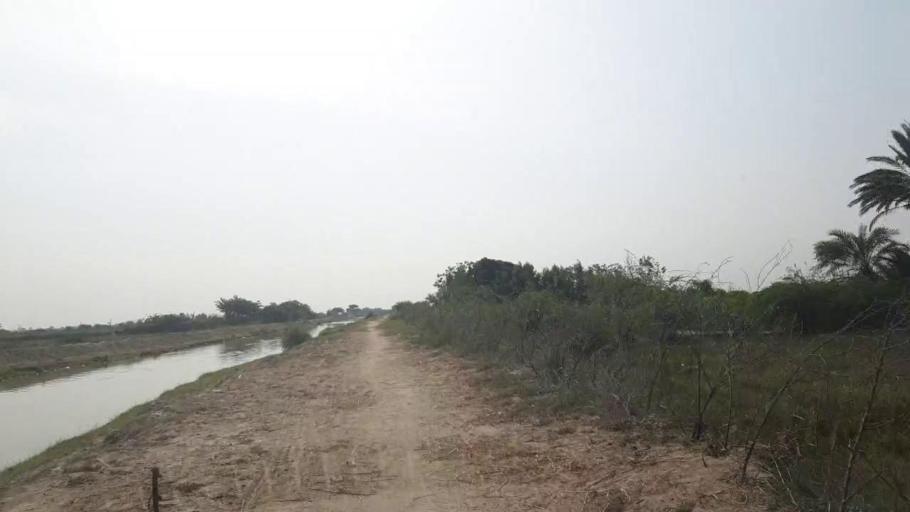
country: PK
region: Sindh
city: Badin
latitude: 24.5604
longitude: 68.8497
